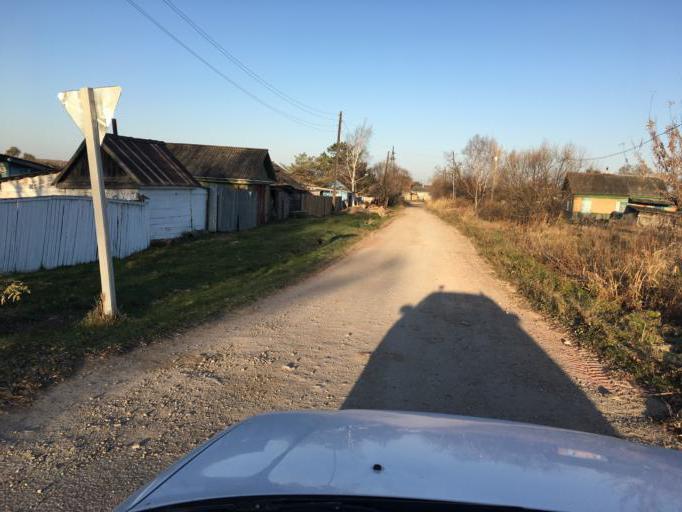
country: RU
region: Primorskiy
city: Lazo
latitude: 45.8638
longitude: 133.6420
